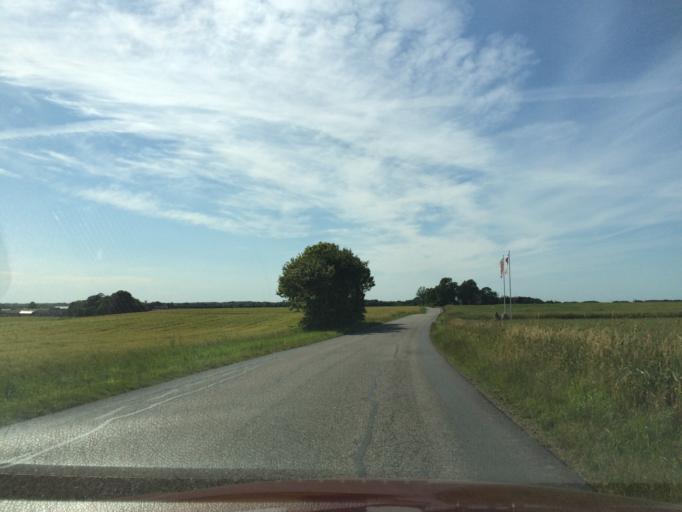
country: DK
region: Central Jutland
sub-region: Silkeborg Kommune
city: Silkeborg
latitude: 56.2261
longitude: 9.6078
